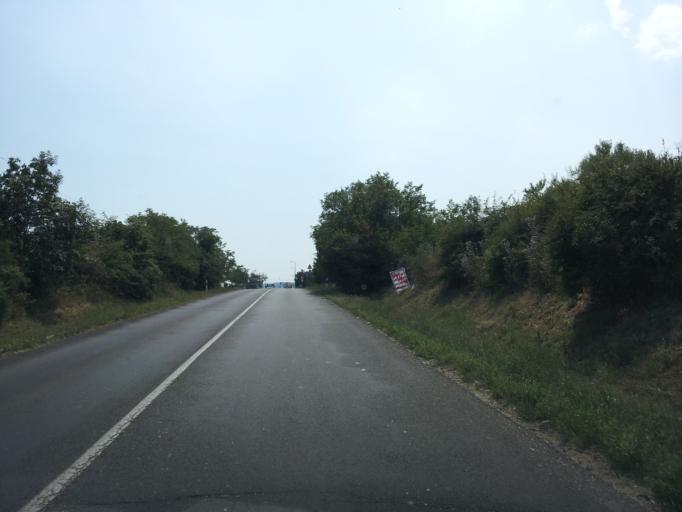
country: HU
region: Veszprem
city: Balatonalmadi
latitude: 47.0630
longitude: 18.0270
